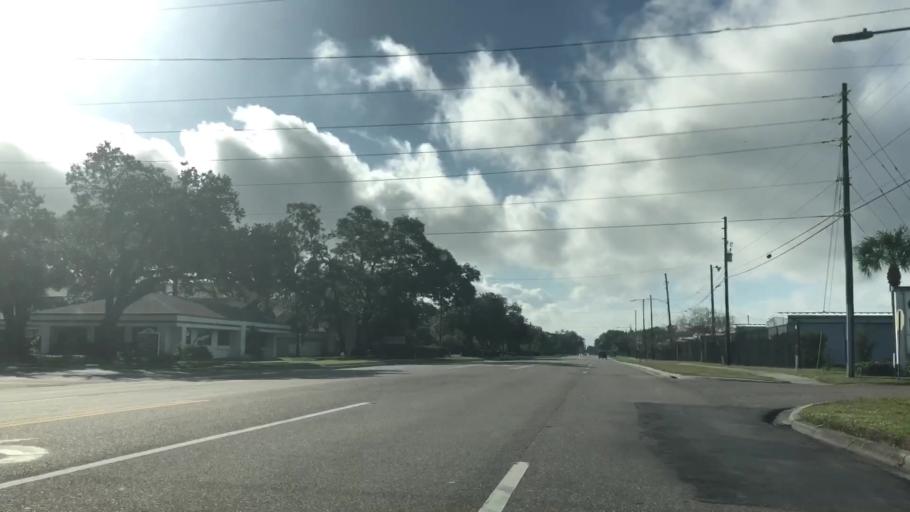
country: US
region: Florida
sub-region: Pinellas County
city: Clearwater
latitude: 27.9754
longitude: -82.7547
